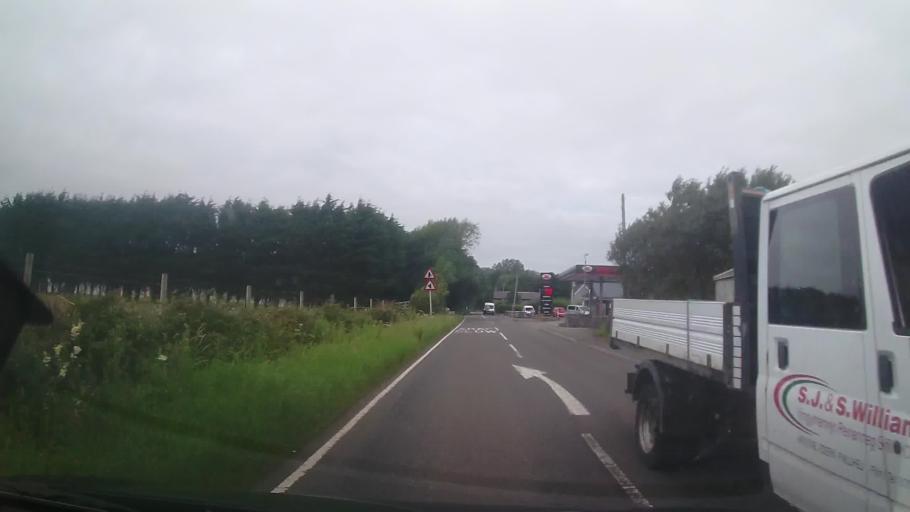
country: GB
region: Wales
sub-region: Gwynedd
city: Caernarfon
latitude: 53.1653
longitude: -4.3328
